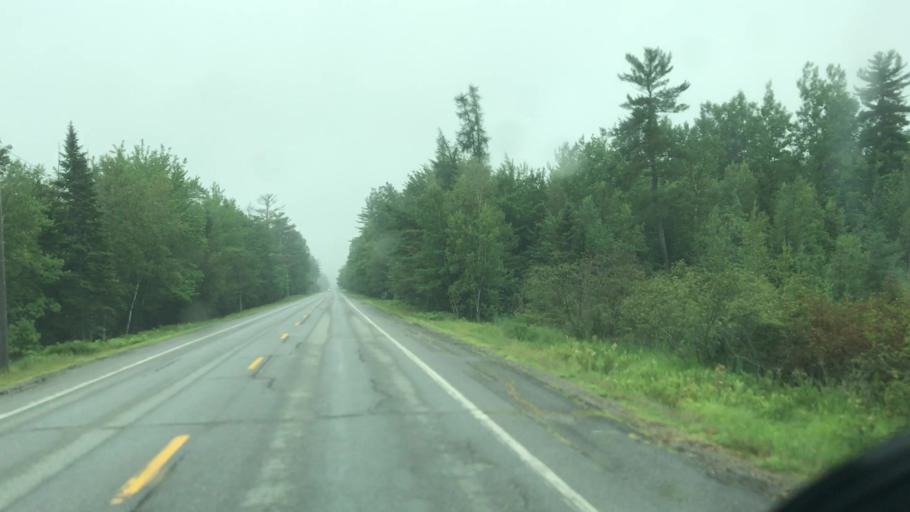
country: US
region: Maine
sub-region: Penobscot County
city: Howland
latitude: 45.2467
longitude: -68.6395
